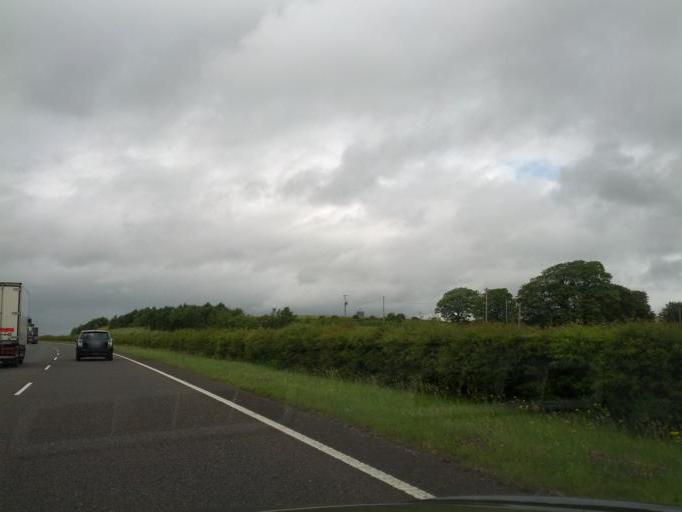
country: IE
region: Munster
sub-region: An Clar
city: Newmarket on Fergus
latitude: 52.7728
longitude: -8.9178
